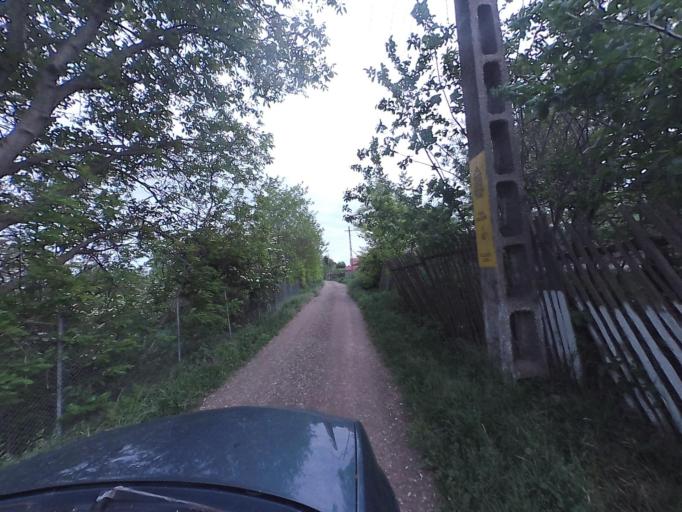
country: RO
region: Neamt
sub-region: Comuna Dulcesti
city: Dulcesti
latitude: 46.9577
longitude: 26.7878
